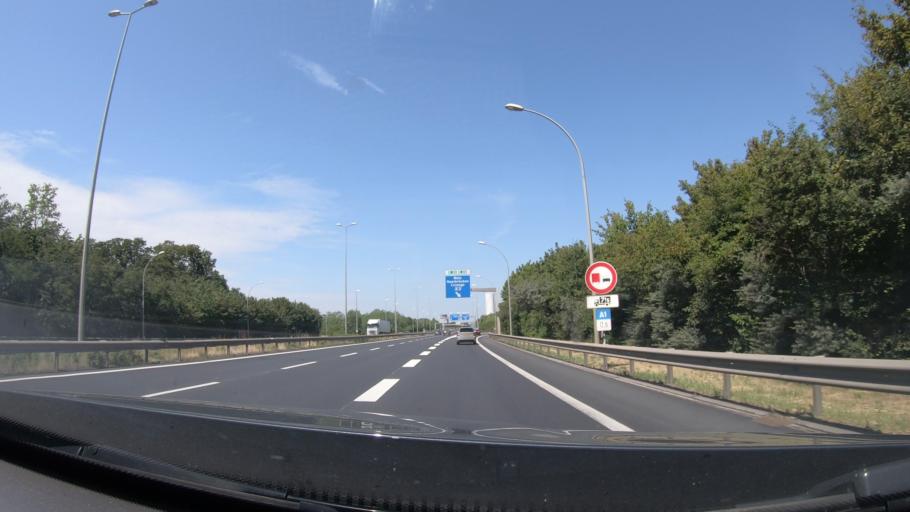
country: LU
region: Luxembourg
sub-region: Canton de Luxembourg
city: Hesperange
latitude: 49.5756
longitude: 6.1310
